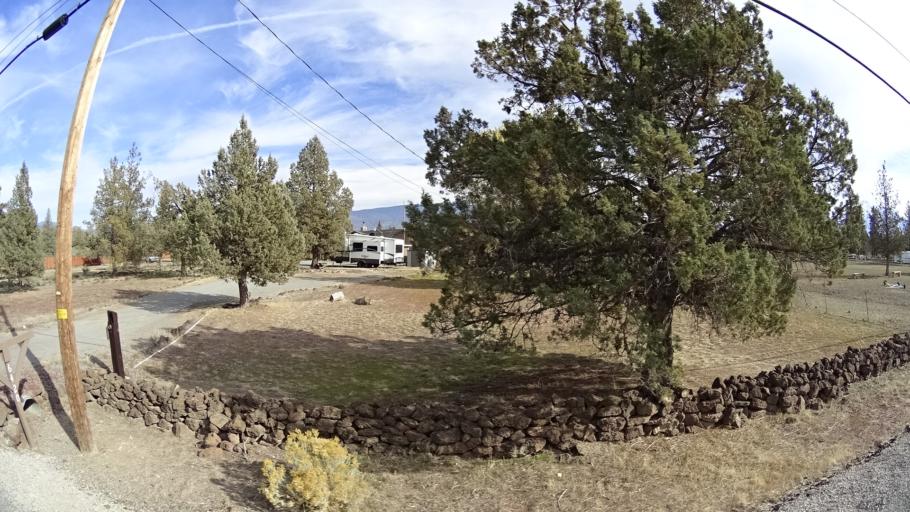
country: US
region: California
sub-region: Siskiyou County
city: Montague
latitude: 41.6508
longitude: -122.3993
